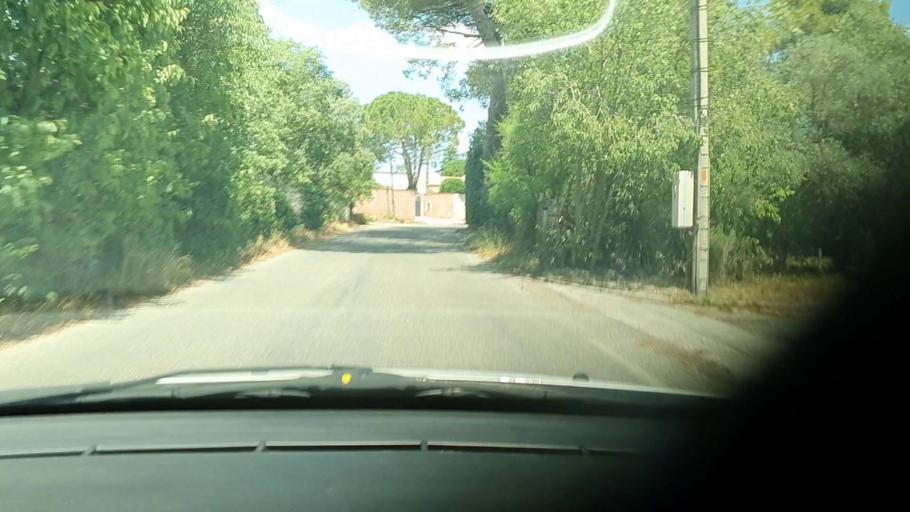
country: FR
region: Languedoc-Roussillon
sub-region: Departement du Gard
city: Uzes
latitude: 44.0163
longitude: 4.3969
